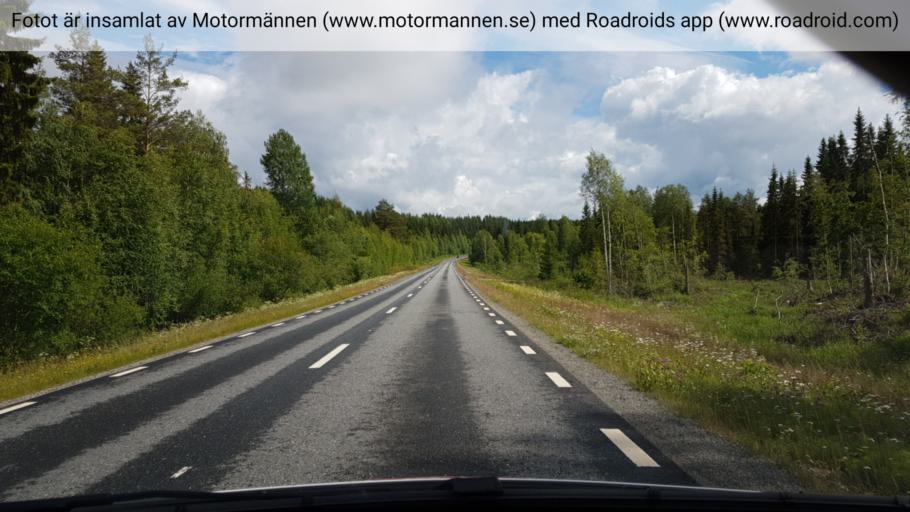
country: SE
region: Vaesterbotten
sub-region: Bjurholms Kommun
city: Bjurholm
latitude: 64.3816
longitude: 19.1254
